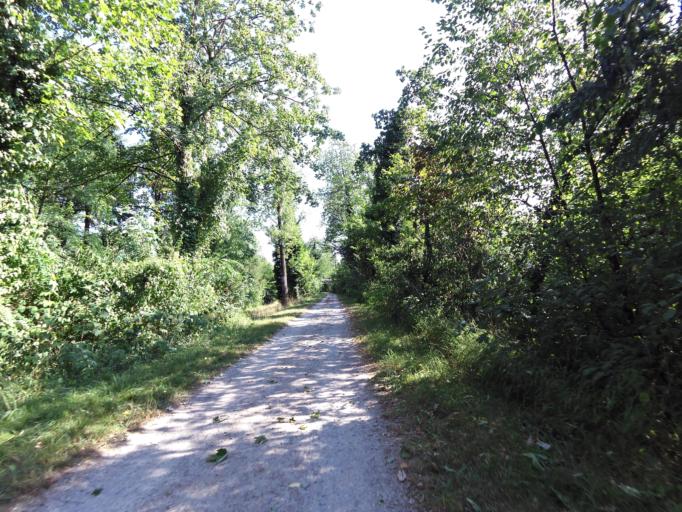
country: CH
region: Aargau
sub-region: Bezirk Brugg
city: Veltheim
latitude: 47.4267
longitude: 8.1636
